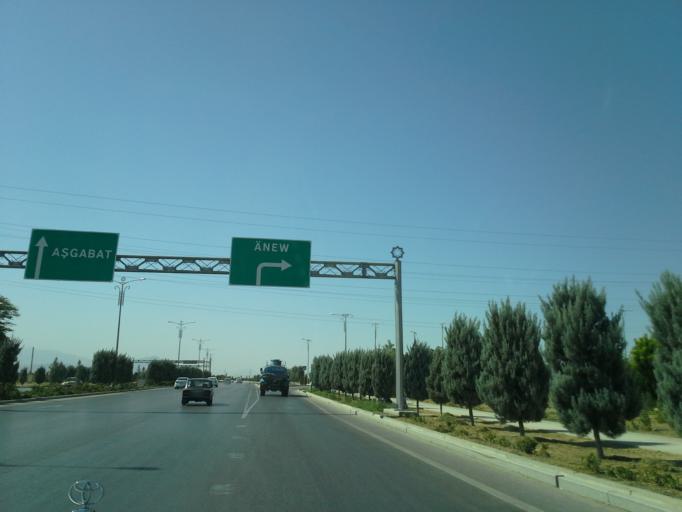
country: TM
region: Ahal
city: Annau
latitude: 37.9132
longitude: 58.4839
